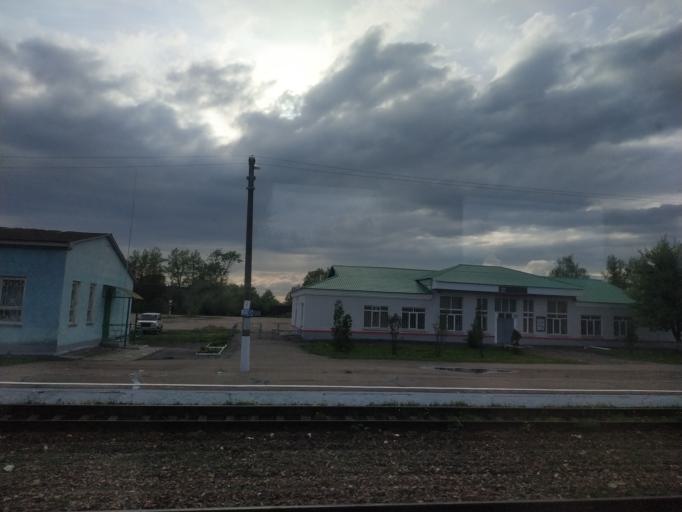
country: RU
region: Smolensk
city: Ugra
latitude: 54.7781
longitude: 34.3424
